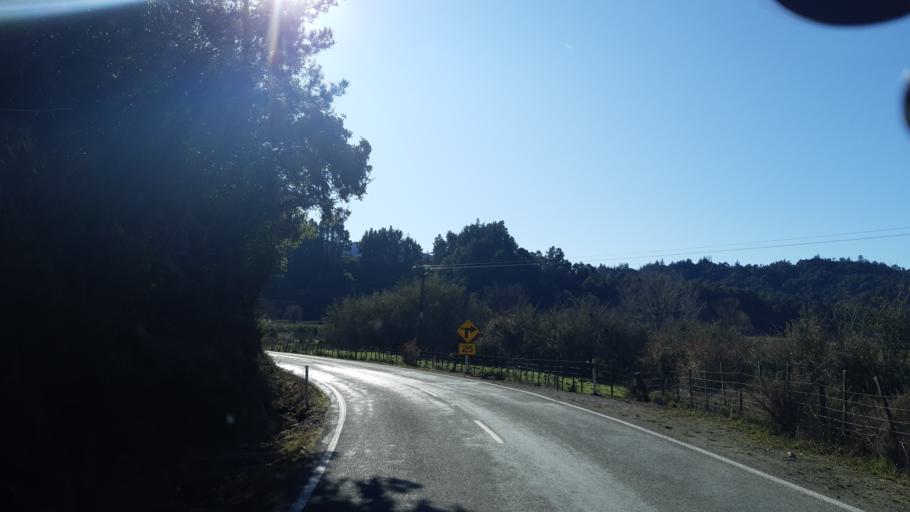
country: NZ
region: Tasman
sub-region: Tasman District
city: Motueka
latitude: -41.0182
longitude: 172.9809
